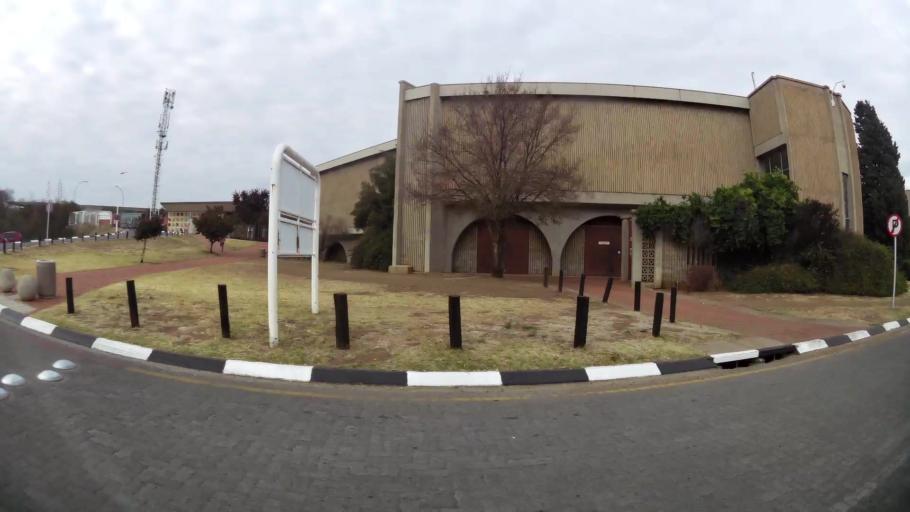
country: ZA
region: Orange Free State
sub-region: Mangaung Metropolitan Municipality
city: Bloemfontein
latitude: -29.1085
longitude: 26.1835
